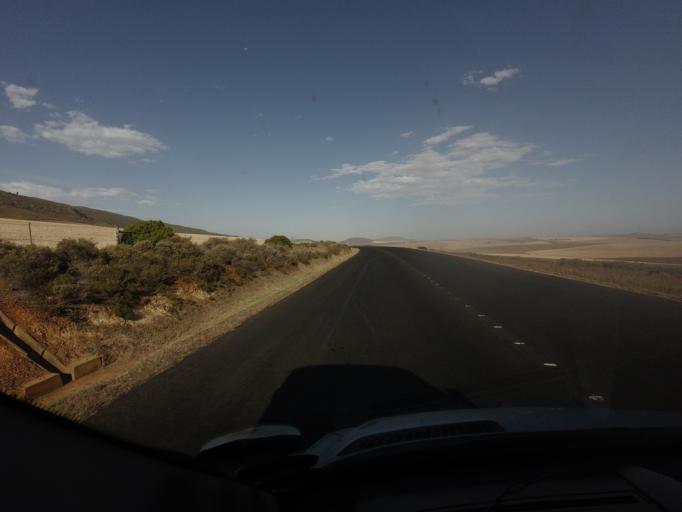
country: ZA
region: Western Cape
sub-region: Overberg District Municipality
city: Swellendam
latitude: -34.1019
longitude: 20.1897
